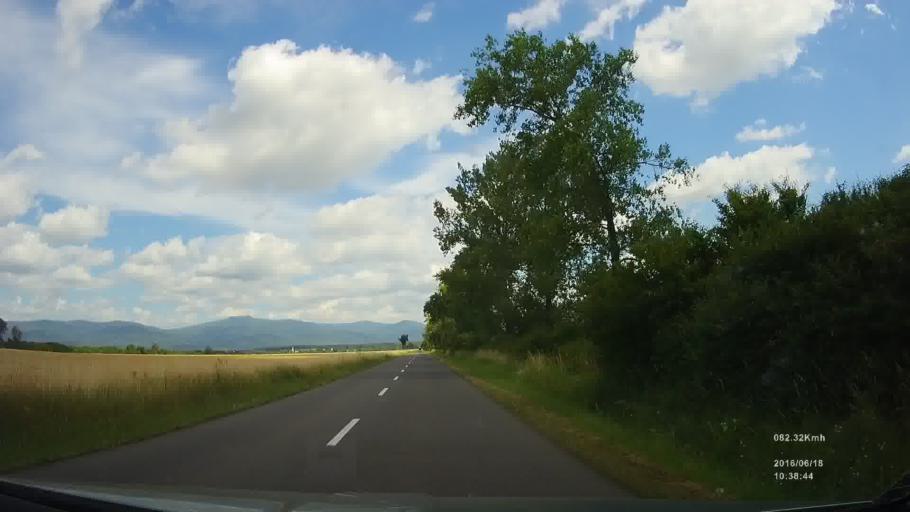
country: SK
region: Kosicky
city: Sobrance
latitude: 48.7648
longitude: 22.1232
